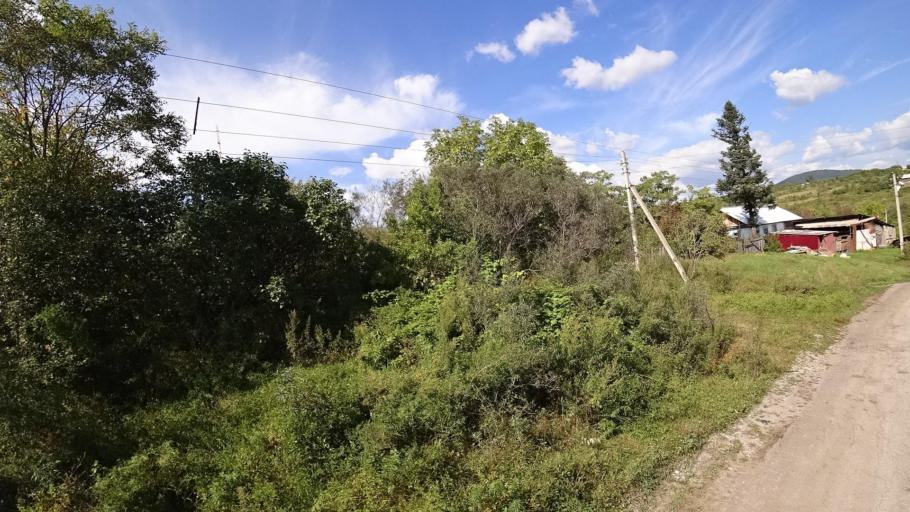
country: RU
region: Jewish Autonomous Oblast
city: Birakan
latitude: 49.0008
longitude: 131.8534
